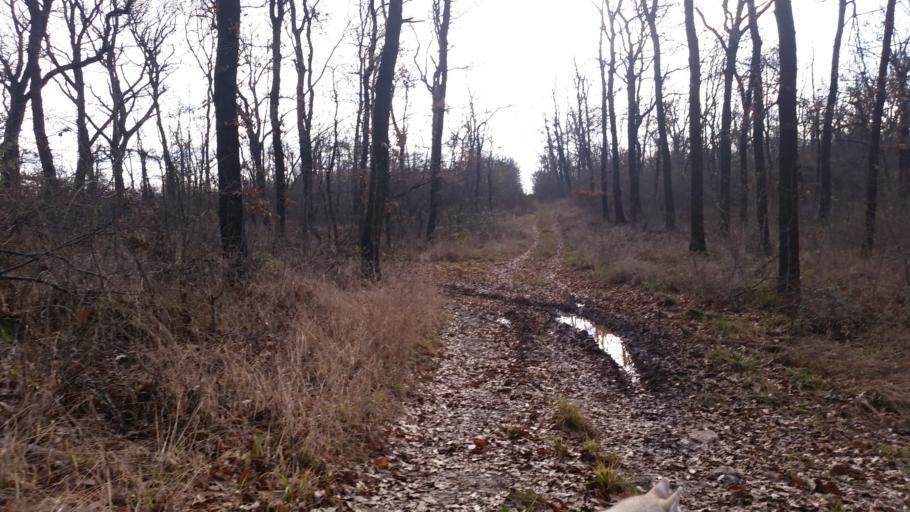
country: HU
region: Pest
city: Telki
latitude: 47.5731
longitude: 18.8302
